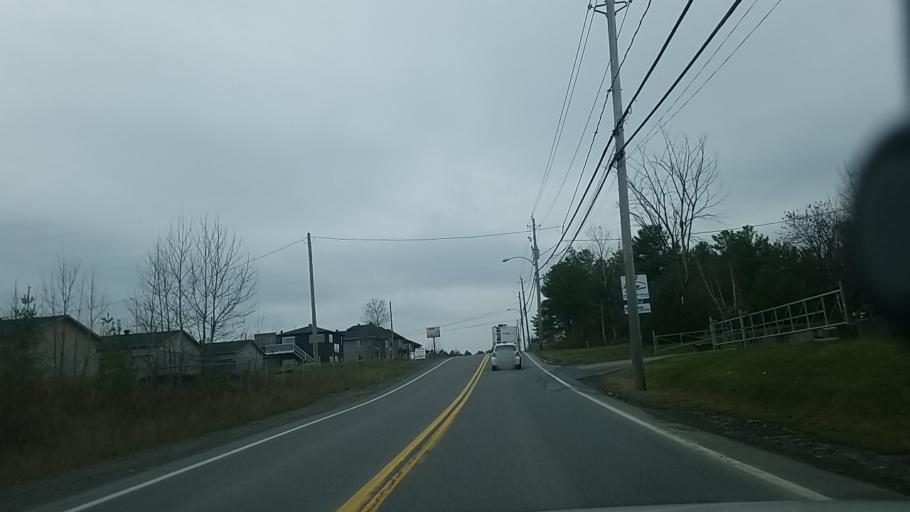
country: CA
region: Quebec
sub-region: Laurentides
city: Saint-Jerome
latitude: 45.7768
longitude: -74.0437
